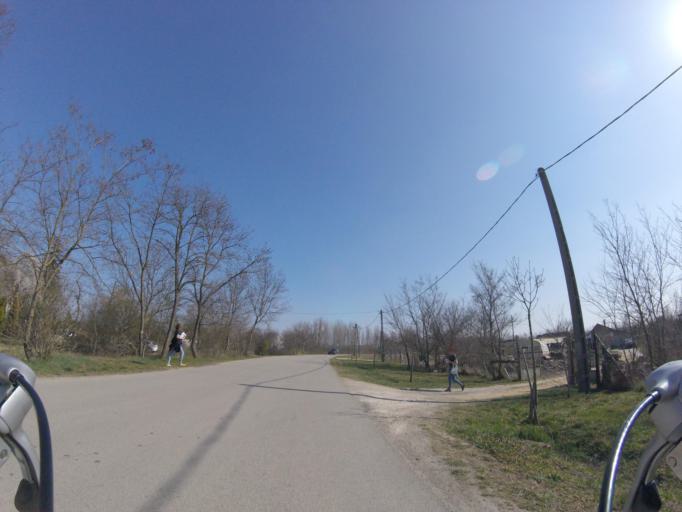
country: HU
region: Fejer
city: Racalmas
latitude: 47.0845
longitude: 18.9357
